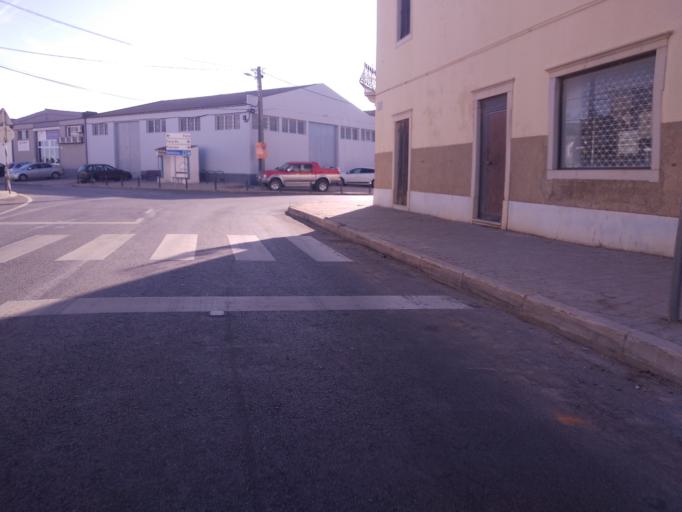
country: PT
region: Faro
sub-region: Faro
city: Faro
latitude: 37.0506
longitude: -7.9373
